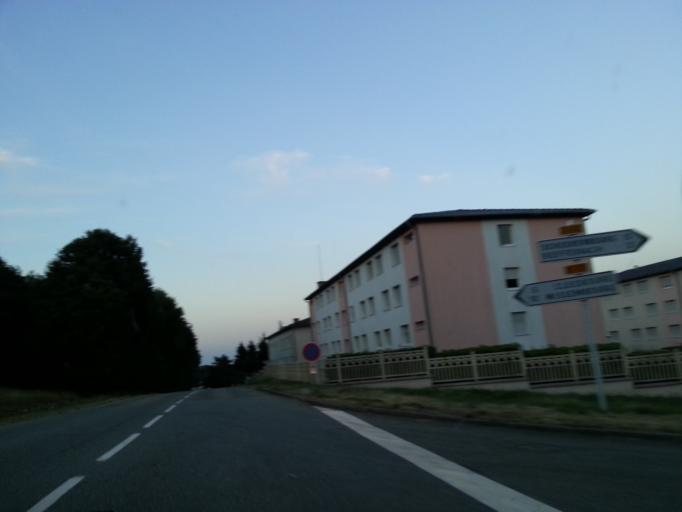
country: FR
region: Alsace
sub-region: Departement du Bas-Rhin
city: Soultz-sous-Forets
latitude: 48.9869
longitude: 7.8567
